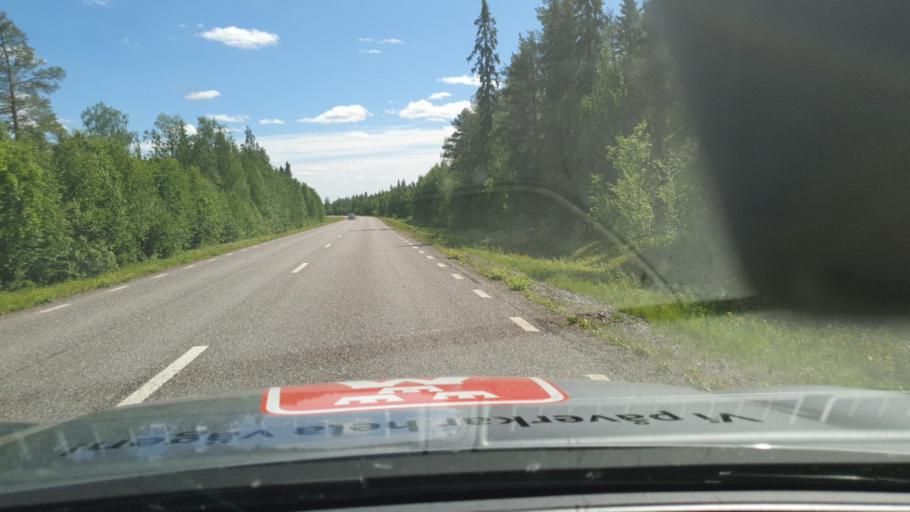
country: SE
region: Norrbotten
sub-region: Pajala Kommun
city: Pajala
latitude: 67.1212
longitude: 23.6035
